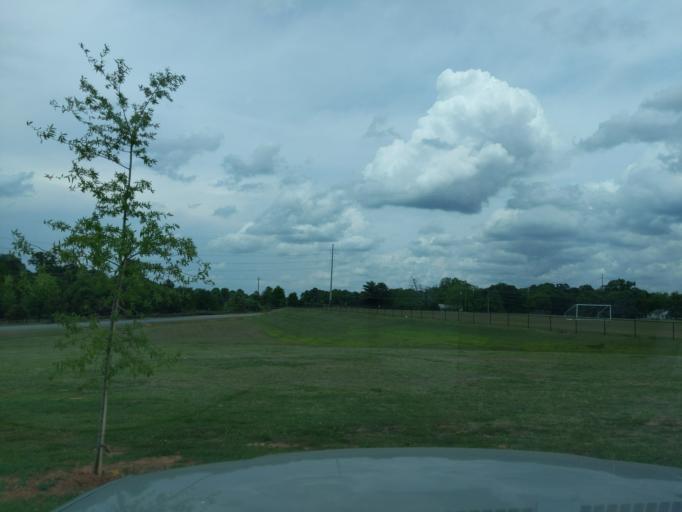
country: US
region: South Carolina
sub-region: Spartanburg County
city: Inman Mills
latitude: 35.0612
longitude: -82.1696
